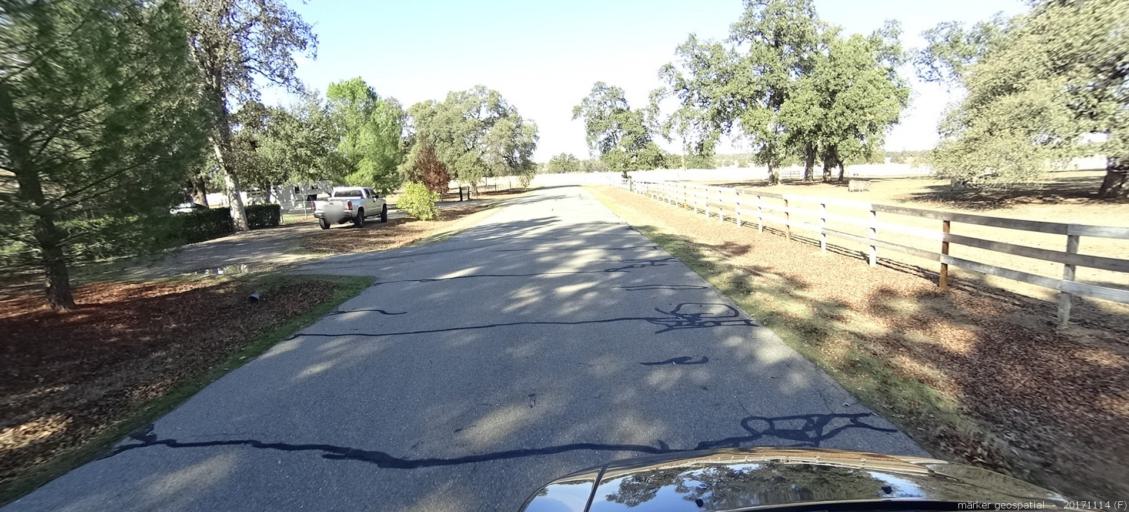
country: US
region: California
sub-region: Shasta County
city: Anderson
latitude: 40.3867
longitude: -122.4662
